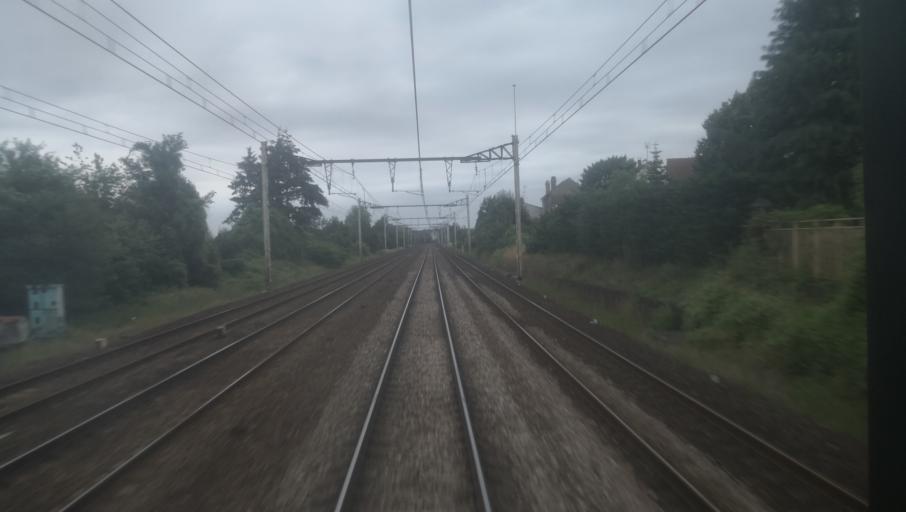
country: FR
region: Ile-de-France
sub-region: Departement de l'Essonne
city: Saint-Michel-sur-Orge
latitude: 48.6375
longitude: 2.3064
